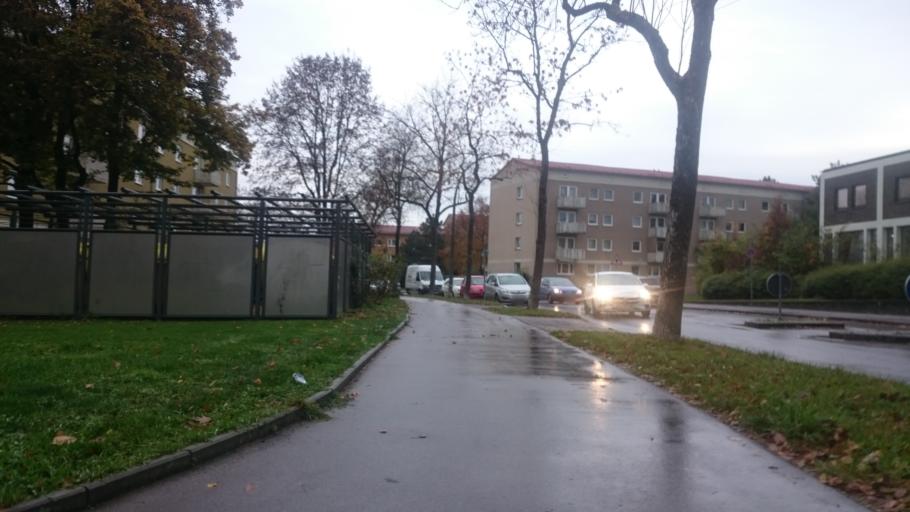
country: DE
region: Bavaria
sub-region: Swabia
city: Augsburg
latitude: 48.3584
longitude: 10.9249
